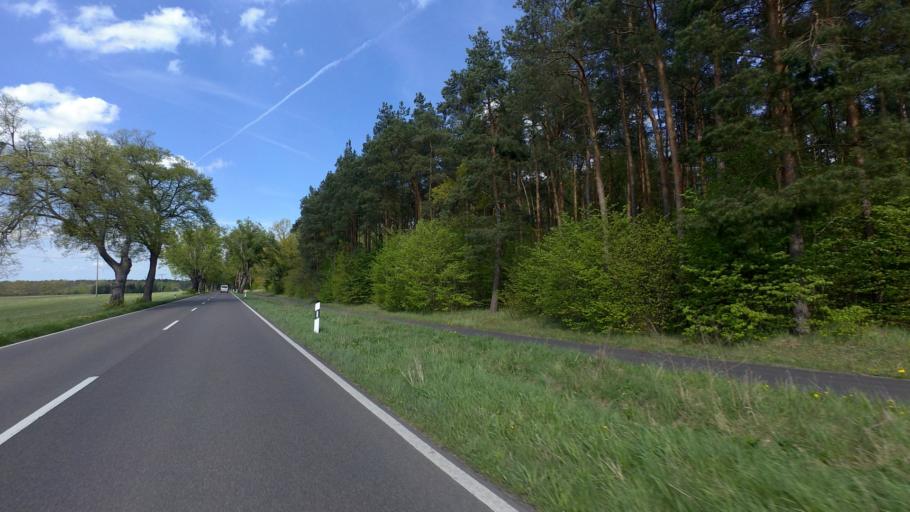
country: DE
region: Brandenburg
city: Milmersdorf
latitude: 53.0666
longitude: 13.6235
